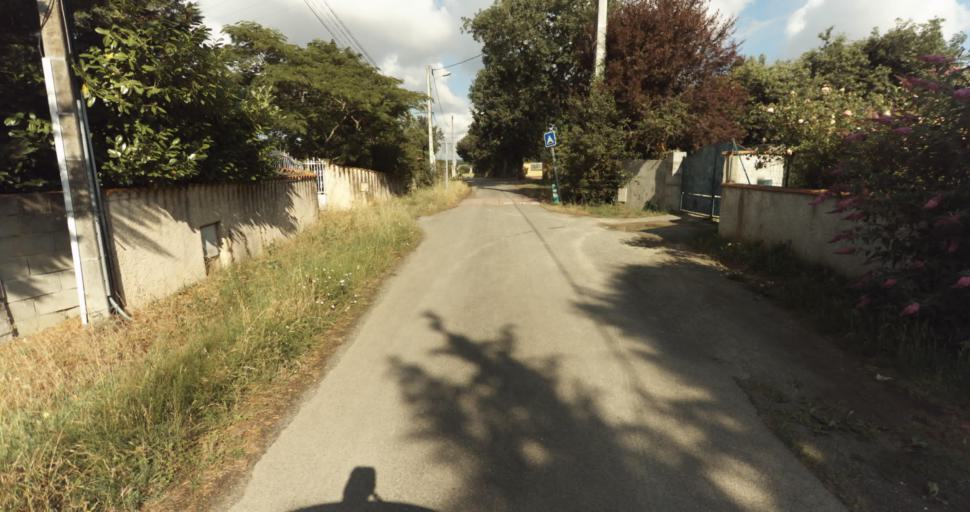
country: FR
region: Midi-Pyrenees
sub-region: Departement de la Haute-Garonne
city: Fontenilles
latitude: 43.5614
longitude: 1.2107
